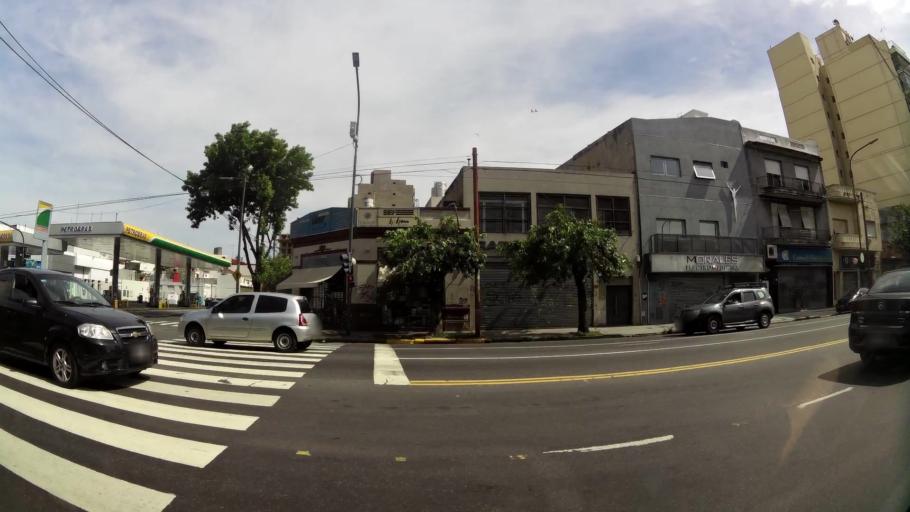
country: AR
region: Buenos Aires F.D.
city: Villa Santa Rita
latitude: -34.6394
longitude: -58.5192
